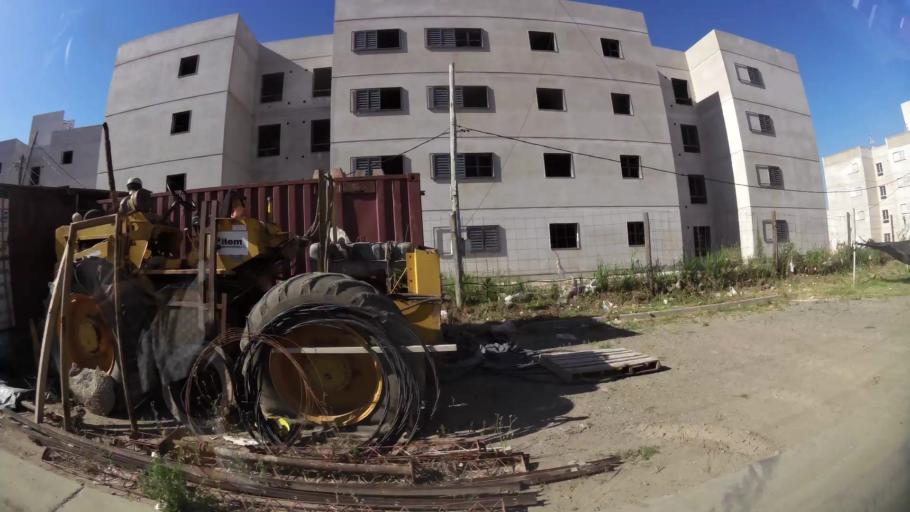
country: AR
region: Cordoba
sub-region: Departamento de Capital
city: Cordoba
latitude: -31.3553
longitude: -64.1935
